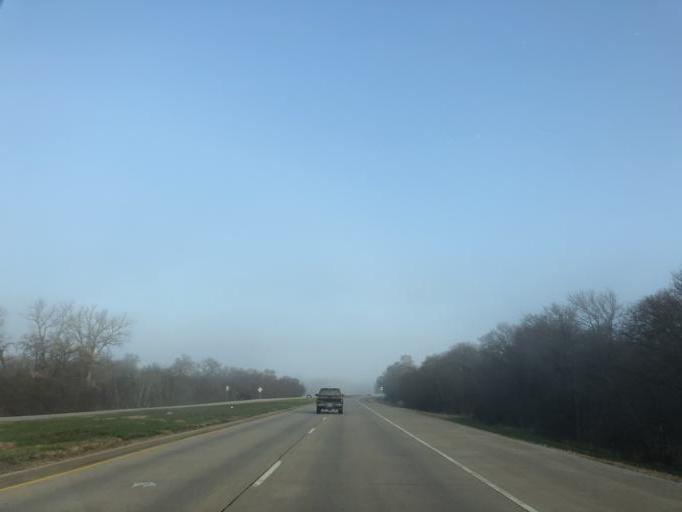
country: US
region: Texas
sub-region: Dallas County
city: Duncanville
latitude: 32.6633
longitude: -96.9830
